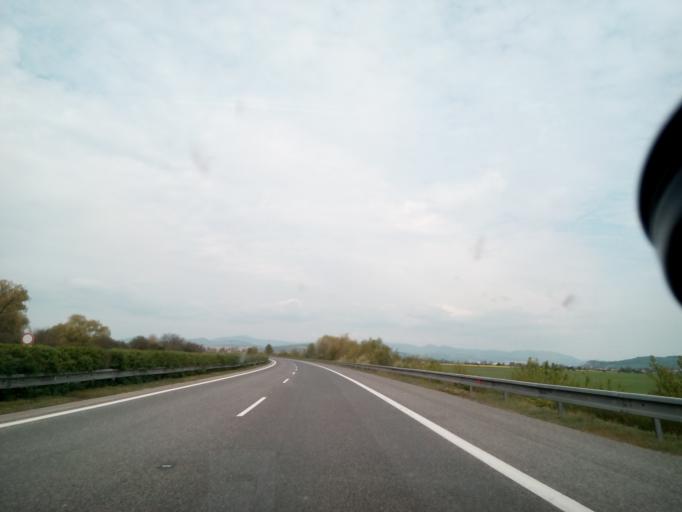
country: SK
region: Trenciansky
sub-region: Okres Nove Mesto nad Vahom
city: Nove Mesto nad Vahom
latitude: 48.7239
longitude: 17.8742
